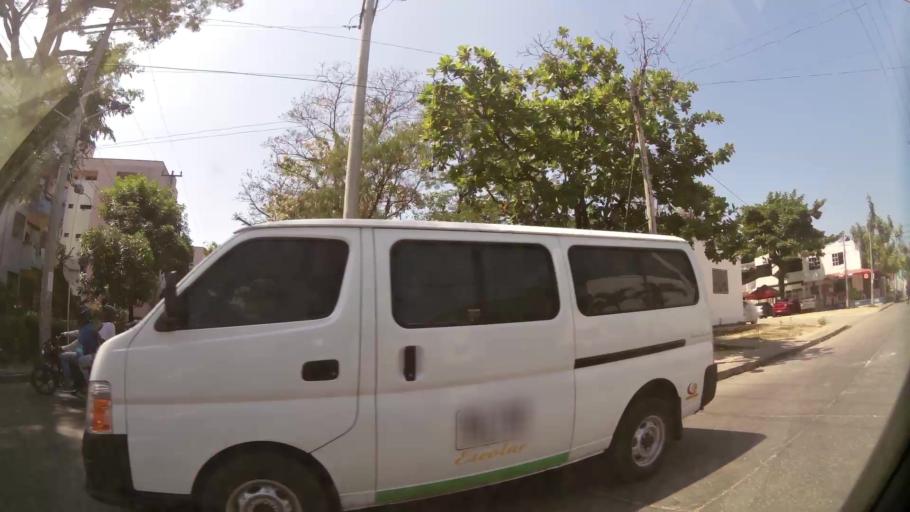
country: CO
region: Bolivar
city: Cartagena
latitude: 10.3984
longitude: -75.4903
